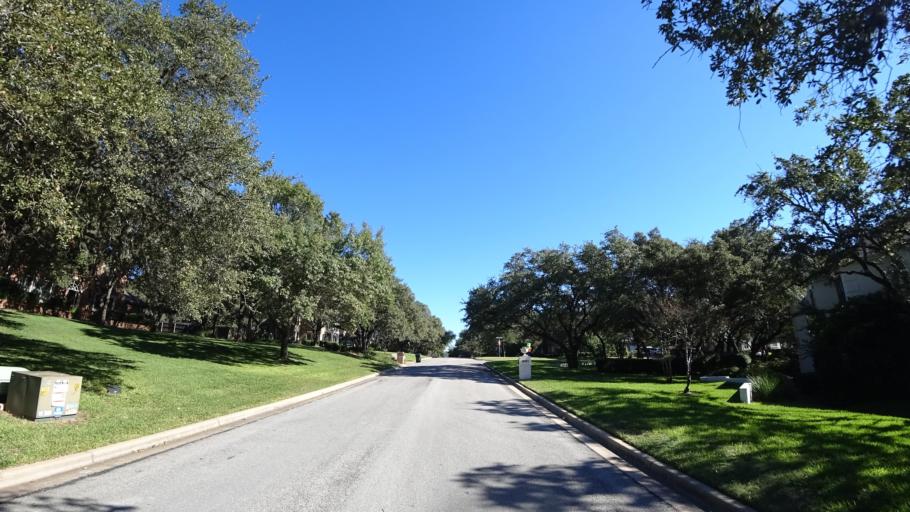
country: US
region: Texas
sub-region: Travis County
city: West Lake Hills
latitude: 30.3323
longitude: -97.7884
